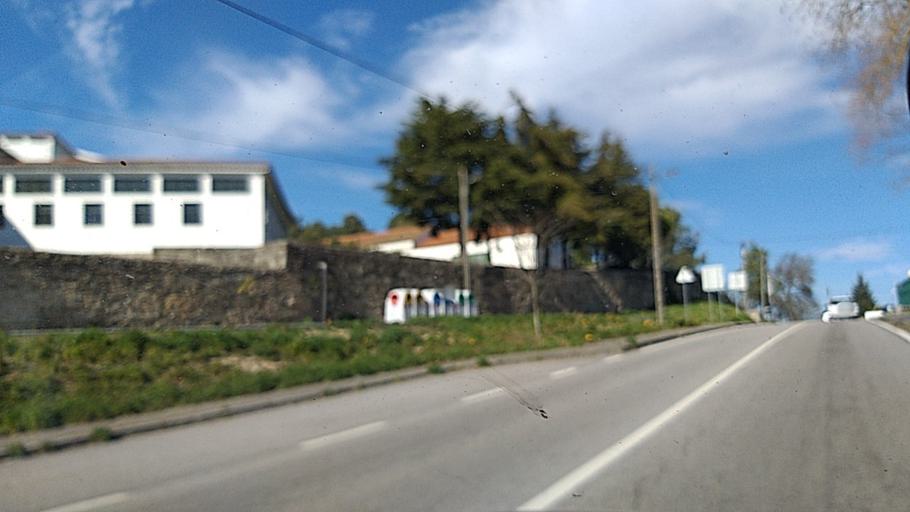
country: PT
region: Guarda
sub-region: Guarda
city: Sequeira
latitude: 40.5658
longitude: -7.2257
